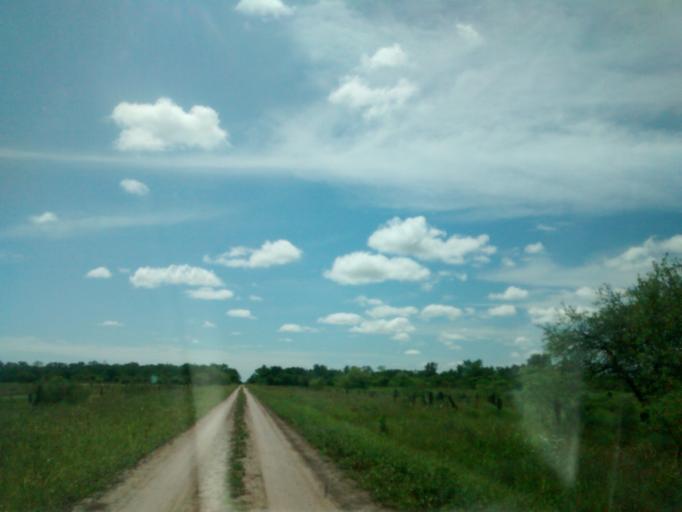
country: AR
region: Chaco
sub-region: Departamento de Quitilipi
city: Quitilipi
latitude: -26.7621
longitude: -60.2838
